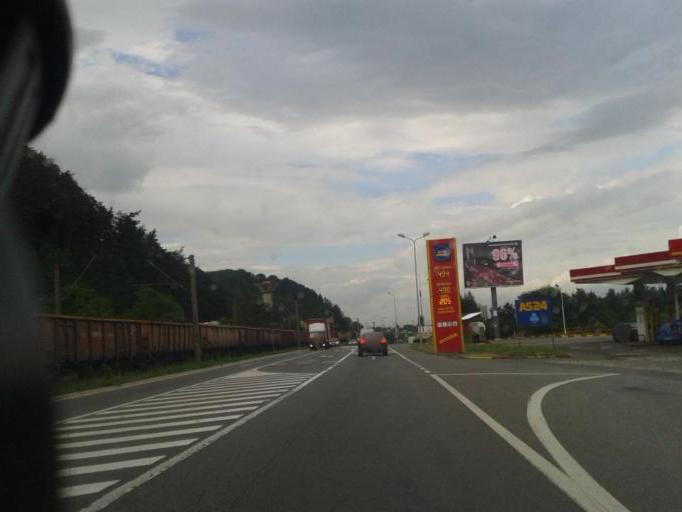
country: RO
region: Brasov
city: Brasov
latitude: 45.6037
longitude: 25.6496
